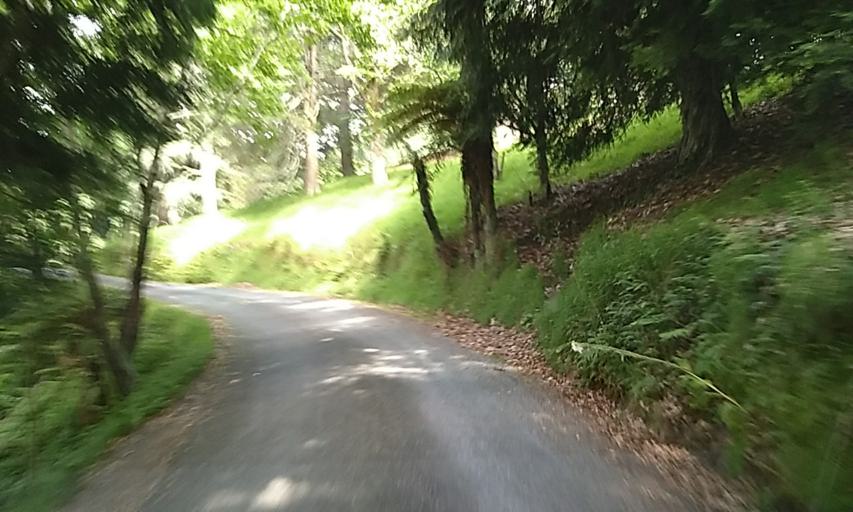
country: NZ
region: Bay of Plenty
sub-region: Tauranga City
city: Tauranga
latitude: -37.8142
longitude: 176.0422
